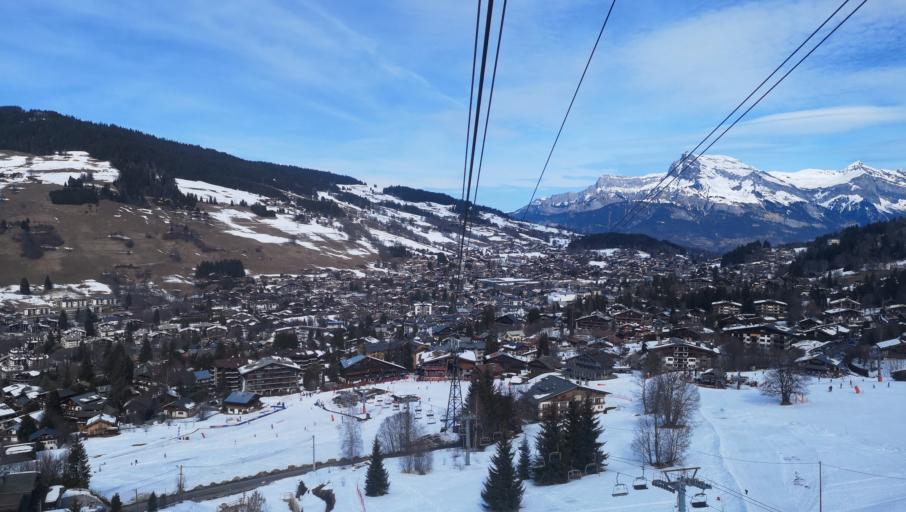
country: FR
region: Rhone-Alpes
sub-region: Departement de la Haute-Savoie
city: Megeve
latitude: 45.8459
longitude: 6.6149
